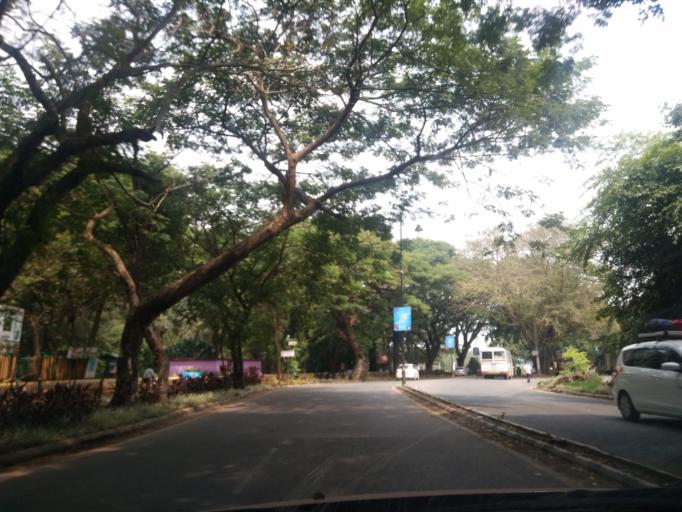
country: IN
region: Goa
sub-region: North Goa
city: Panaji
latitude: 15.4976
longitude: 73.8193
